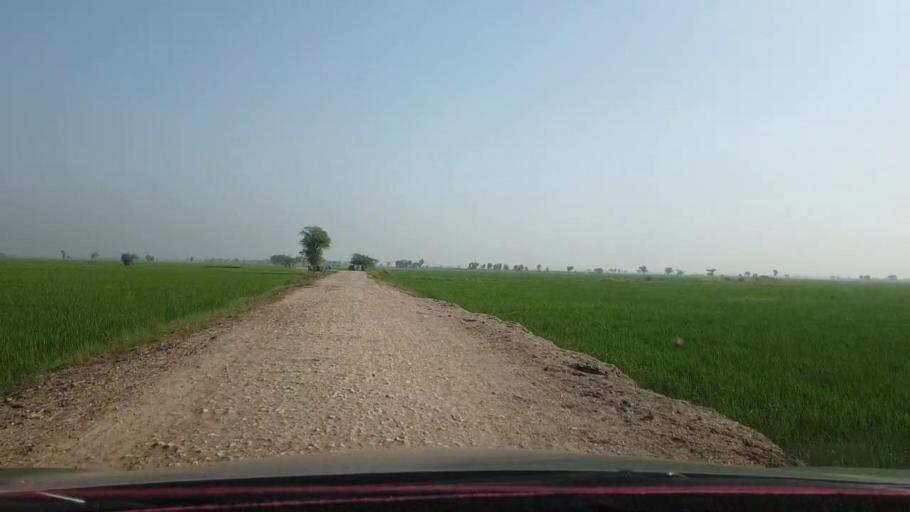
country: PK
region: Sindh
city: Nasirabad
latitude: 27.4654
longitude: 67.9204
